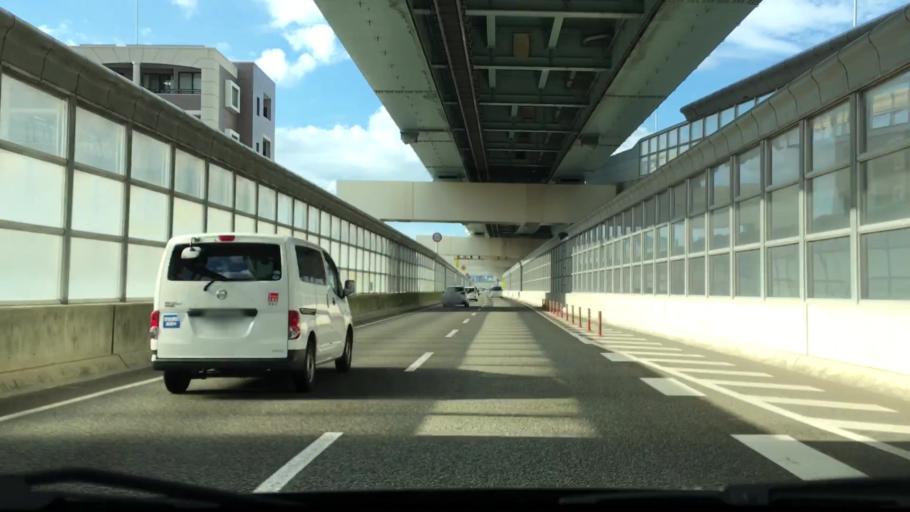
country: JP
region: Fukuoka
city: Fukuoka-shi
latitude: 33.5720
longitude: 130.3166
